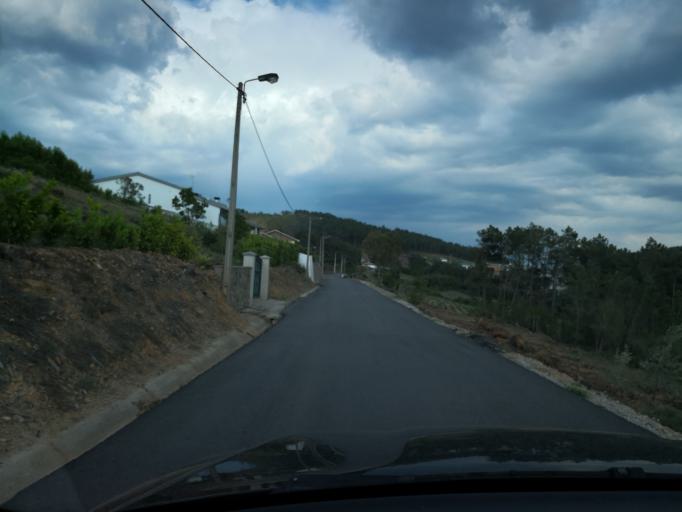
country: PT
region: Vila Real
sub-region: Sabrosa
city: Vilela
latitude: 41.2217
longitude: -7.6801
